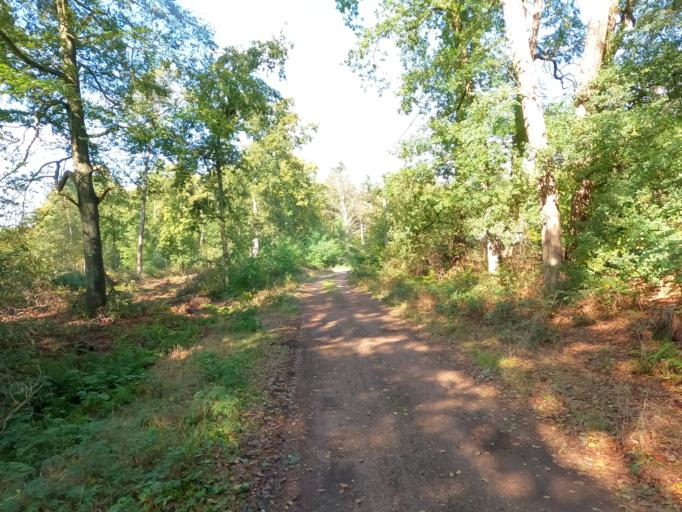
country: BE
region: Flanders
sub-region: Provincie Antwerpen
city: Oostmalle
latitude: 51.2668
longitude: 4.7707
